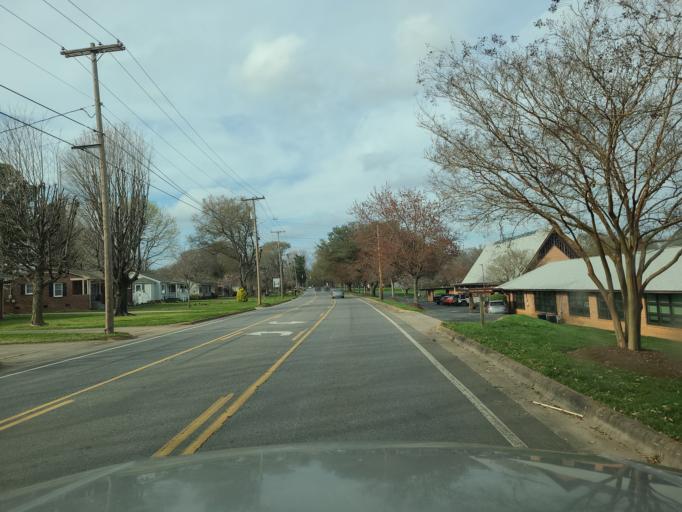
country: US
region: North Carolina
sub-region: Cleveland County
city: Shelby
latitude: 35.2850
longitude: -81.5619
